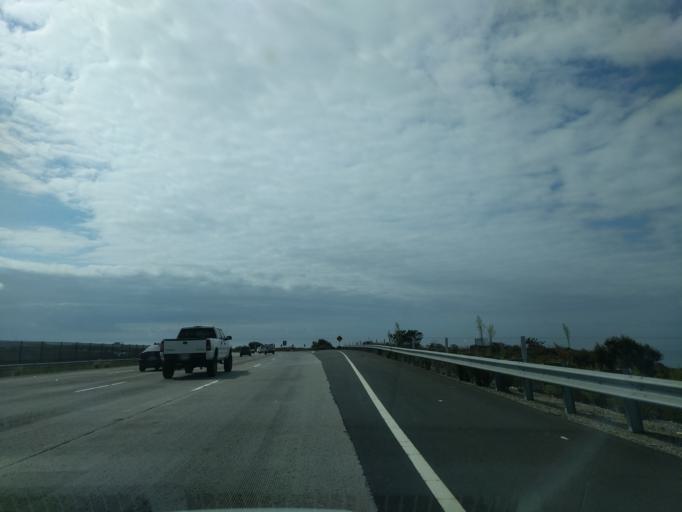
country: US
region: California
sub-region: San Diego County
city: Camp Pendleton South
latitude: 33.3159
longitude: -117.4826
